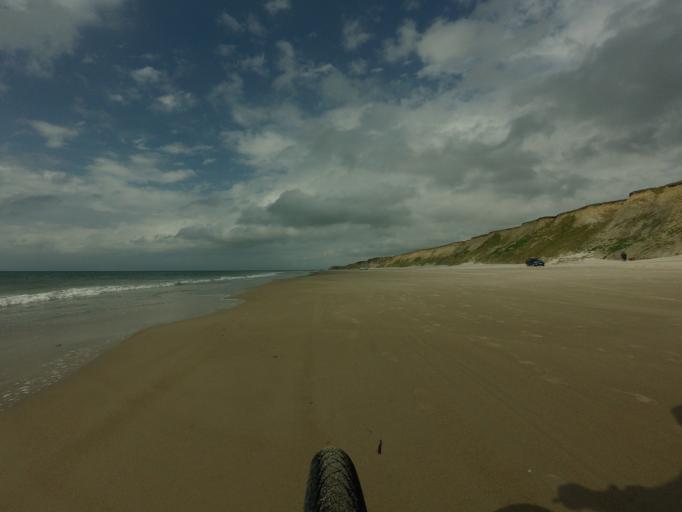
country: DK
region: North Denmark
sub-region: Jammerbugt Kommune
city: Pandrup
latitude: 57.3983
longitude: 9.7330
